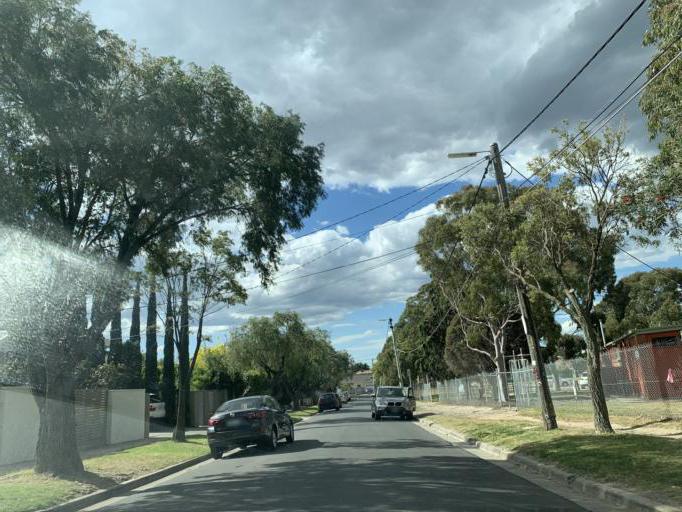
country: AU
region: Victoria
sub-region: Bayside
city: Hampton
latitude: -37.9395
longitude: 145.0164
